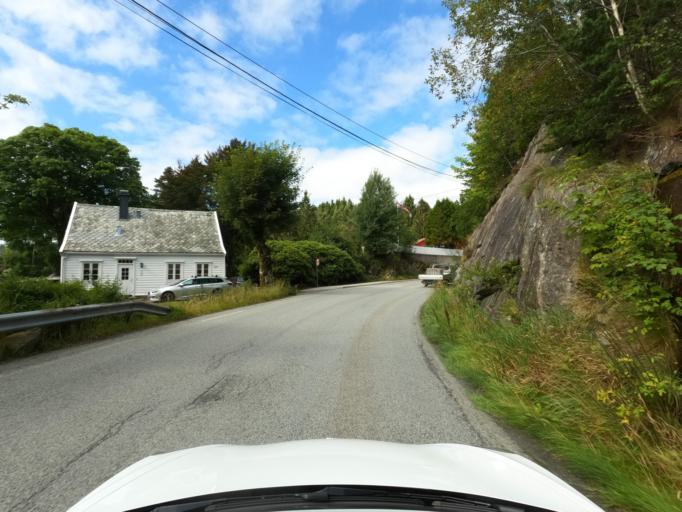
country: NO
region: Hordaland
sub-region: Os
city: Syfteland
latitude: 60.2677
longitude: 5.3684
